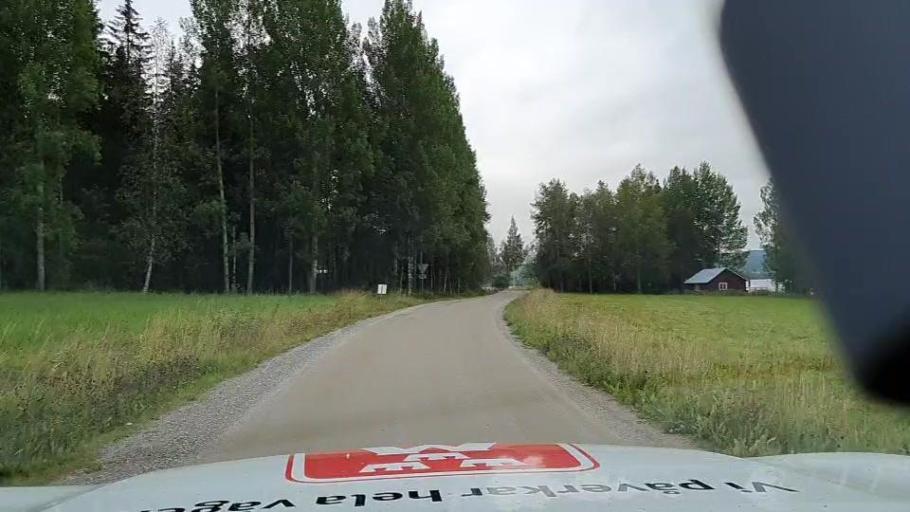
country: SE
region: Jaemtland
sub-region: Ragunda Kommun
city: Hammarstrand
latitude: 63.1706
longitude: 15.8203
